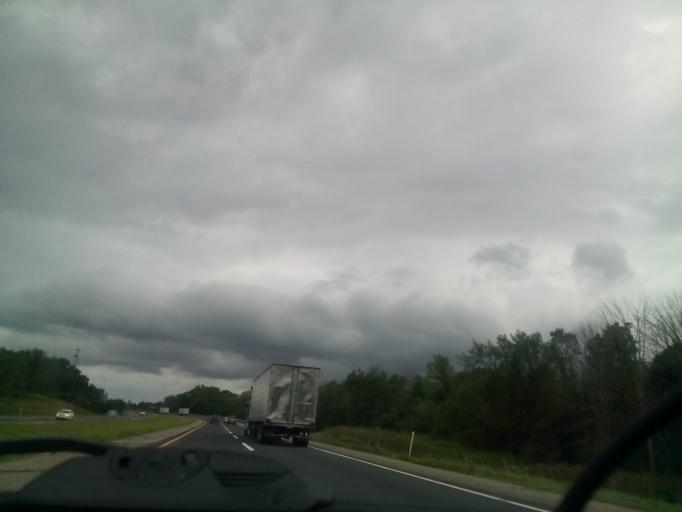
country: US
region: Indiana
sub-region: Steuben County
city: Fremont
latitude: 41.6519
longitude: -84.8436
